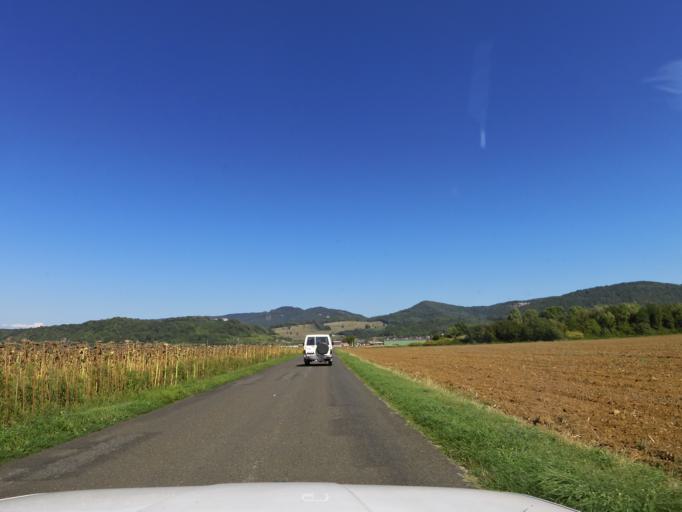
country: FR
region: Rhone-Alpes
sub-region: Departement de l'Ain
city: Saint-Denis-en-Bugey
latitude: 45.9238
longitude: 5.3269
